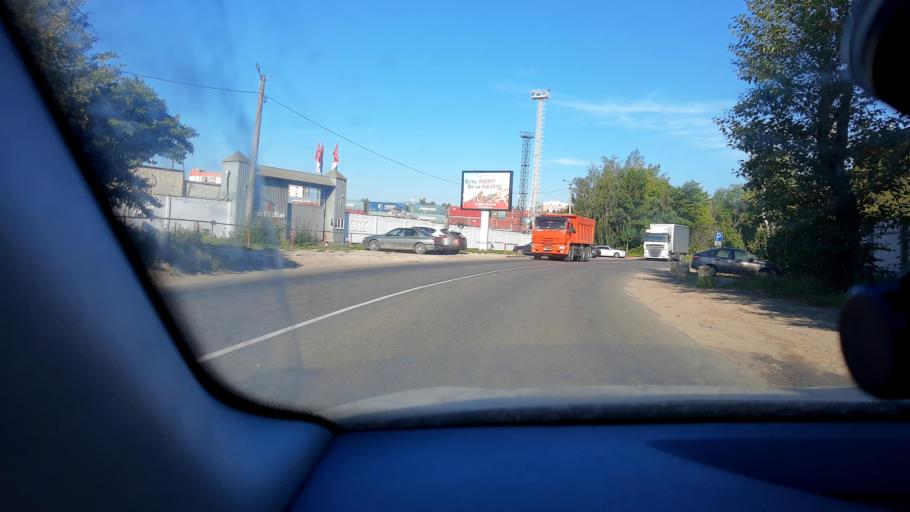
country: RU
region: Moskovskaya
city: Shcherbinka
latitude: 55.4669
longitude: 37.5661
